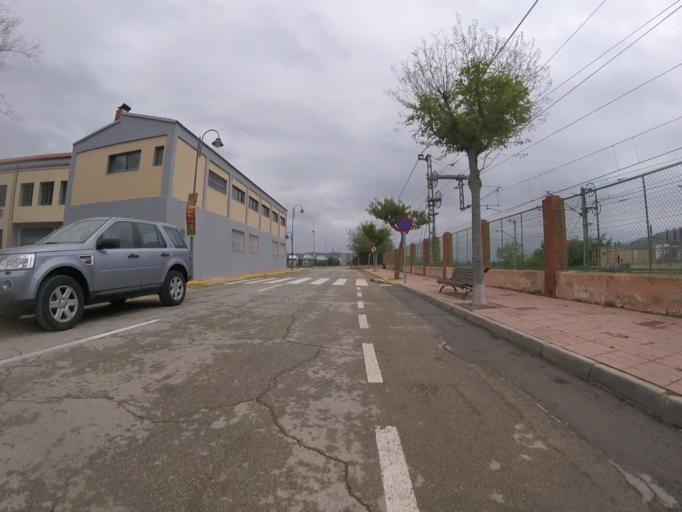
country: ES
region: Valencia
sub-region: Provincia de Castello
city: Alcala de Xivert
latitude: 40.3056
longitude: 0.2291
